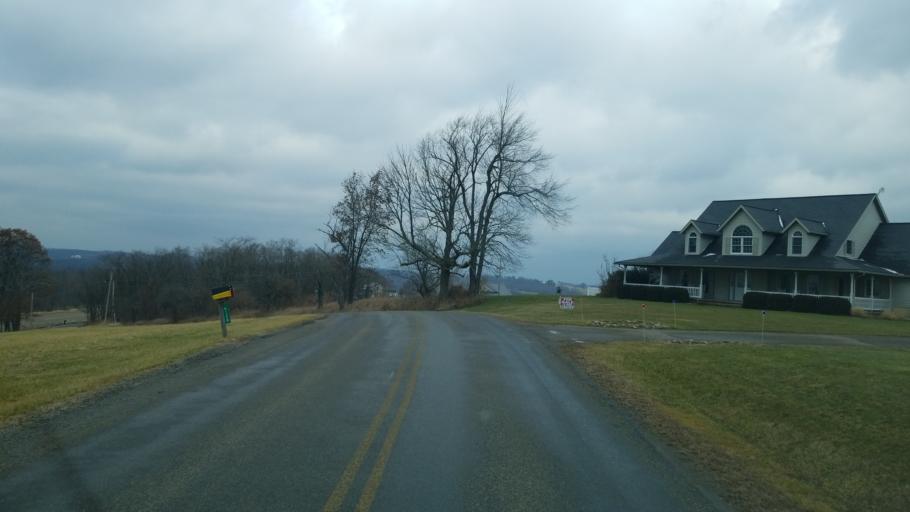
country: US
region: Ohio
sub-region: Holmes County
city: Millersburg
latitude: 40.5826
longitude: -81.9654
